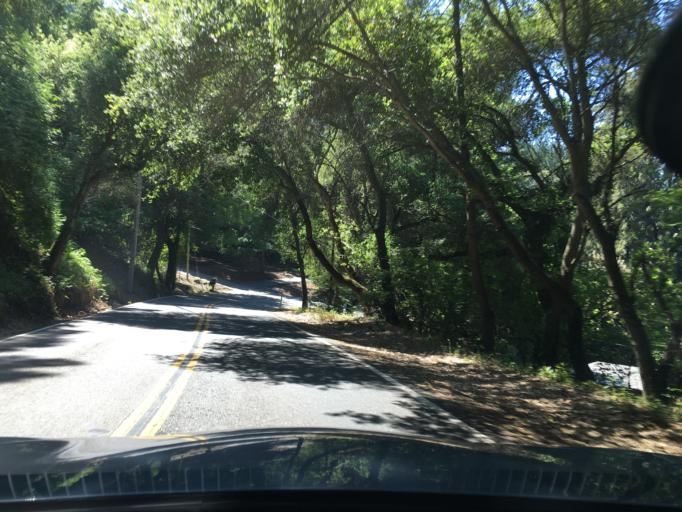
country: US
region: California
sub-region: Santa Clara County
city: Lexington Hills
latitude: 37.1619
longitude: -121.9830
